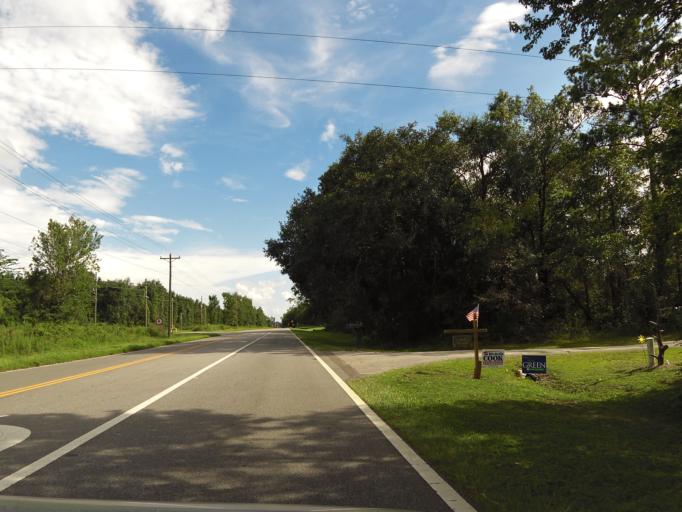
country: US
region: Florida
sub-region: Clay County
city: Green Cove Springs
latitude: 29.9594
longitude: -81.6936
